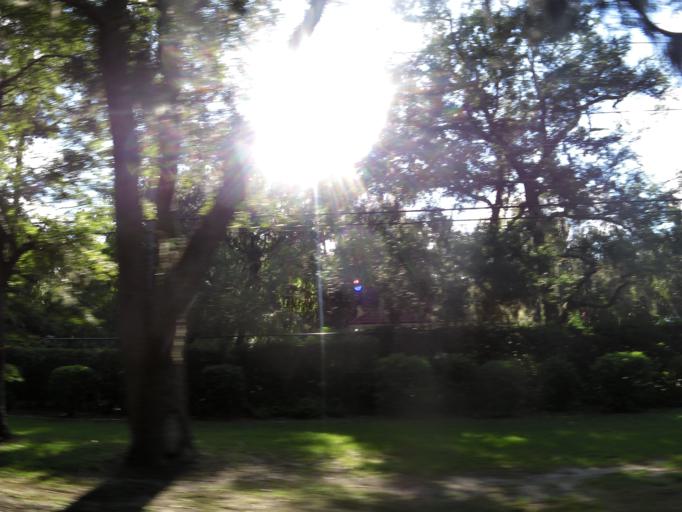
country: US
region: Georgia
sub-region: Glynn County
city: Saint Simon Mills
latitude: 31.2026
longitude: -81.3760
